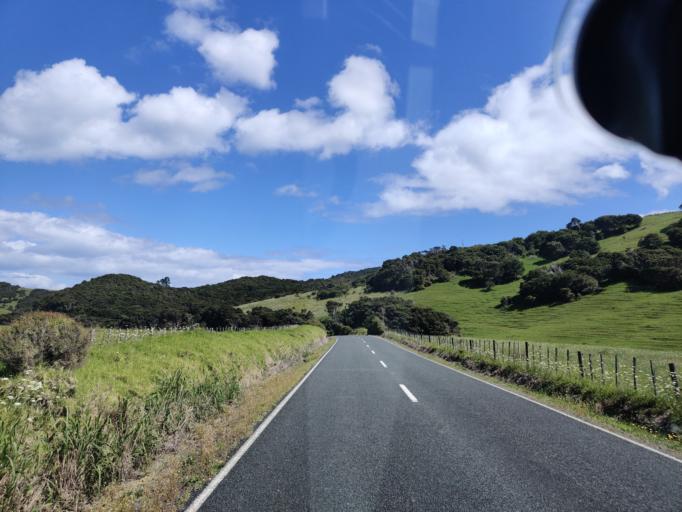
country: NZ
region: Northland
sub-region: Far North District
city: Paihia
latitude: -35.2705
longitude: 174.2783
